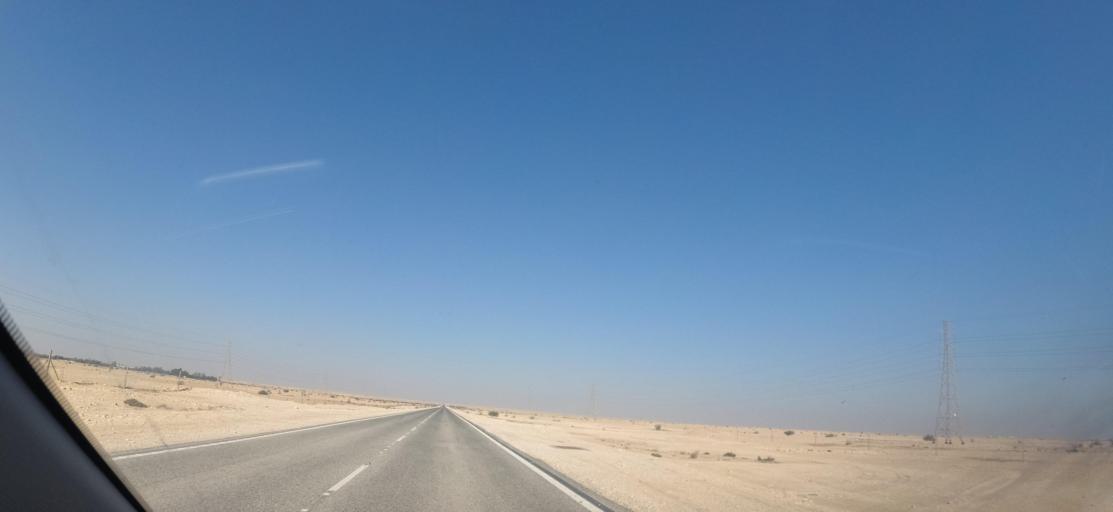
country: QA
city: Al Jumayliyah
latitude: 25.6628
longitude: 51.1216
